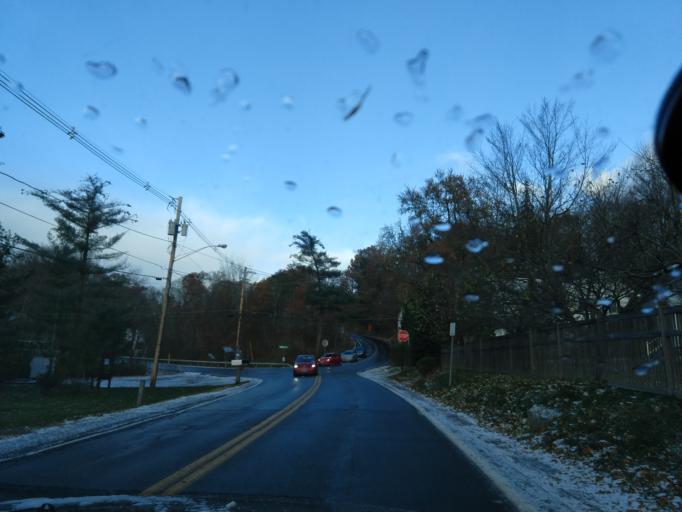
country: US
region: New York
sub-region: Tompkins County
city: East Ithaca
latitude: 42.4530
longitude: -76.4695
